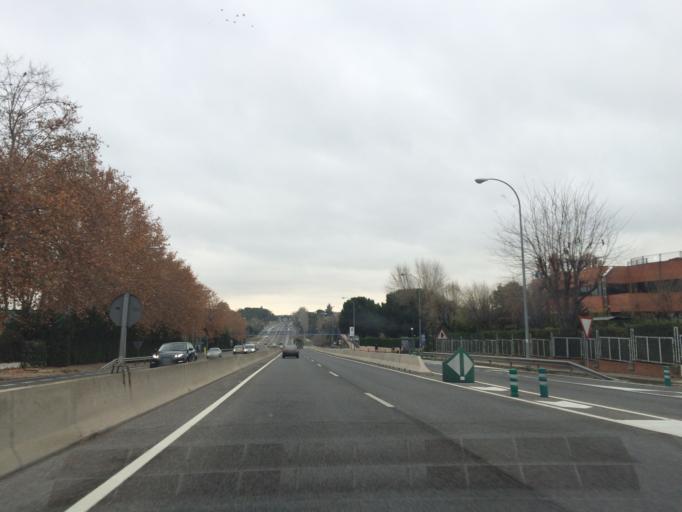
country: ES
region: Madrid
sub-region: Provincia de Madrid
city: Moncloa-Aravaca
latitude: 40.4568
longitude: -3.7682
